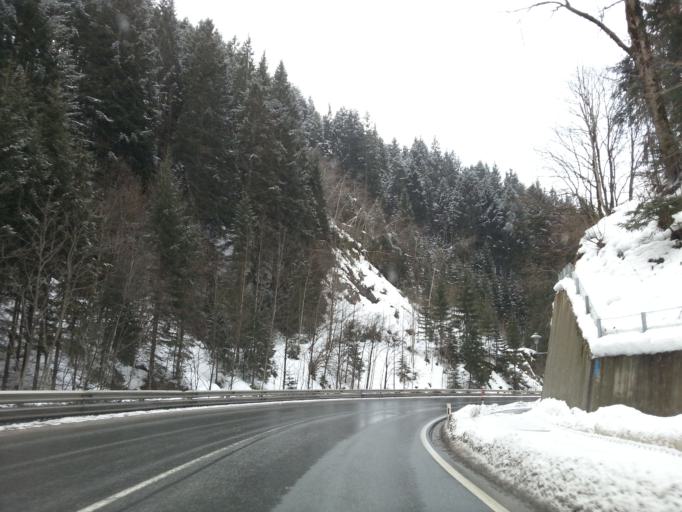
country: AT
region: Salzburg
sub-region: Politischer Bezirk Sankt Johann im Pongau
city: Eben im Pongau
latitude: 47.4338
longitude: 13.3567
